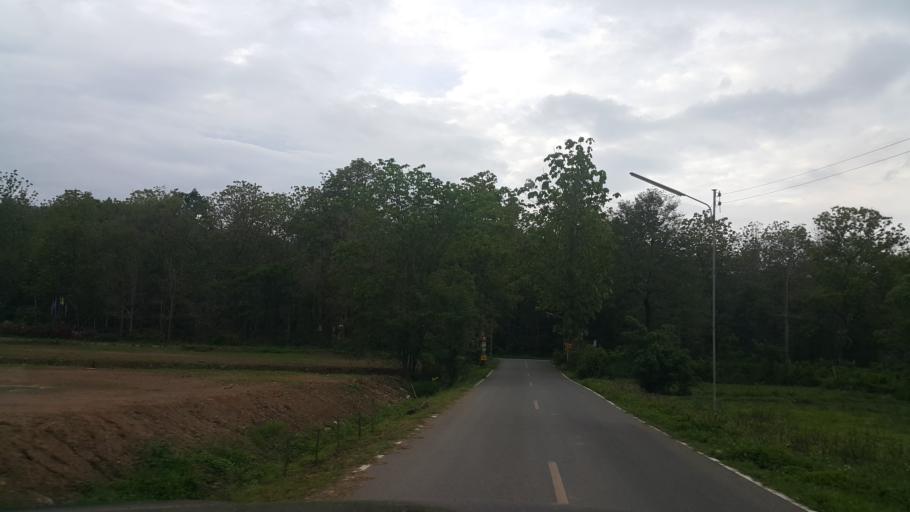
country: TH
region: Chiang Mai
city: Mae On
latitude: 18.7415
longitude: 99.2195
